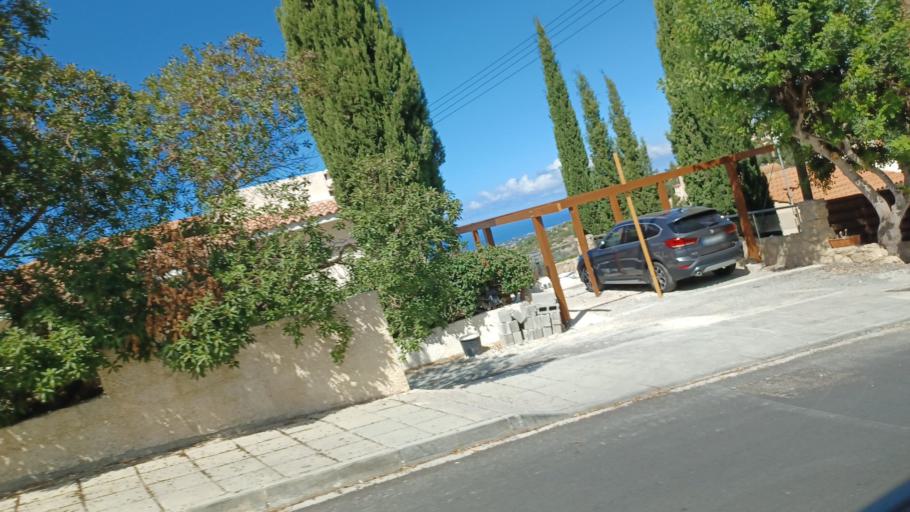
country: CY
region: Pafos
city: Tala
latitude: 34.8463
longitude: 32.4324
